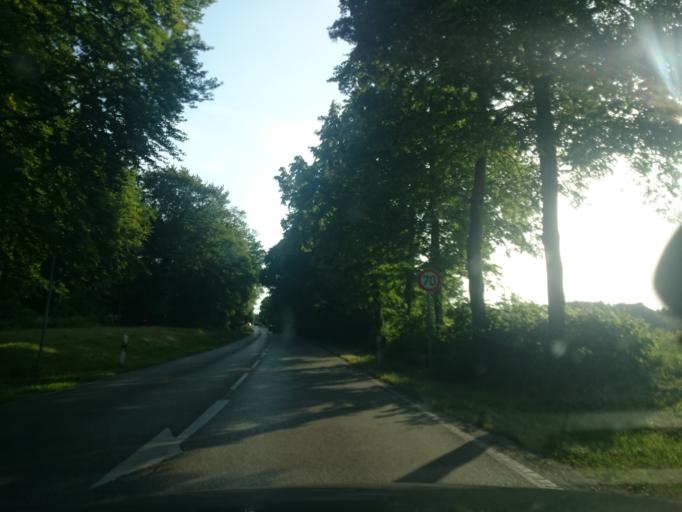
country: DE
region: Bavaria
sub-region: Upper Bavaria
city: Wessling
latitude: 48.0815
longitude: 11.2645
